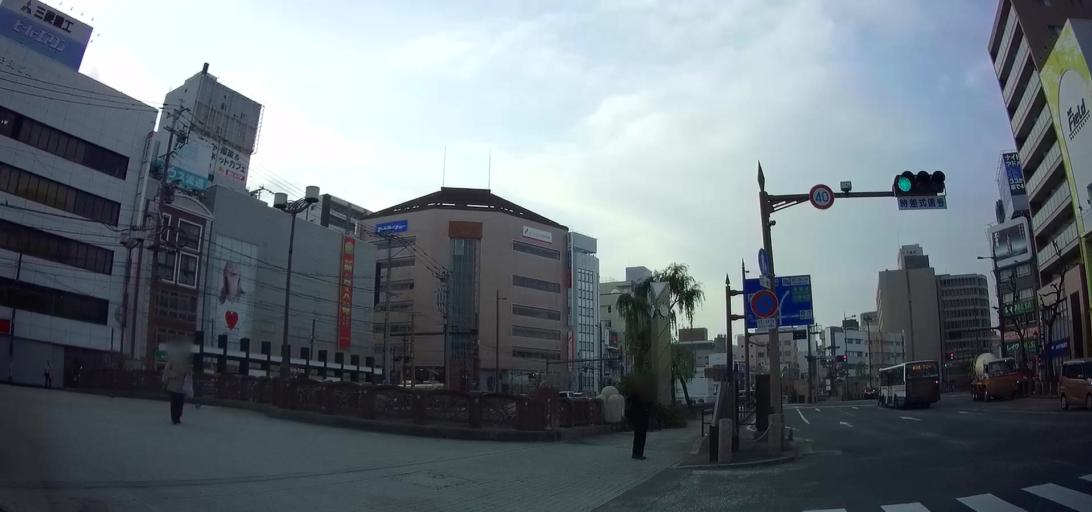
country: JP
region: Nagasaki
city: Nagasaki-shi
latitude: 32.7449
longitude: 129.8763
